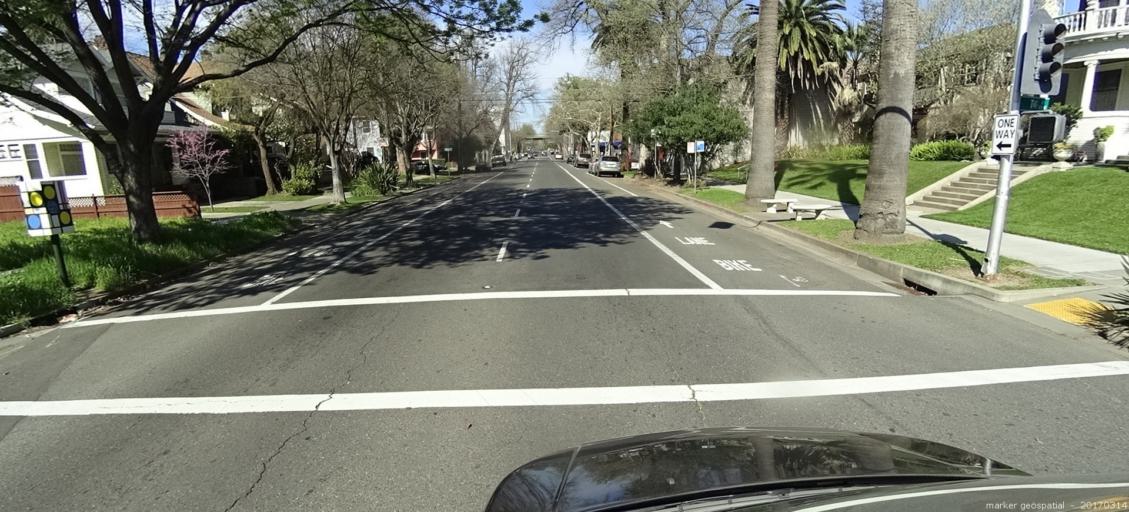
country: US
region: California
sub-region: Sacramento County
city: Sacramento
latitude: 38.5652
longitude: -121.4834
